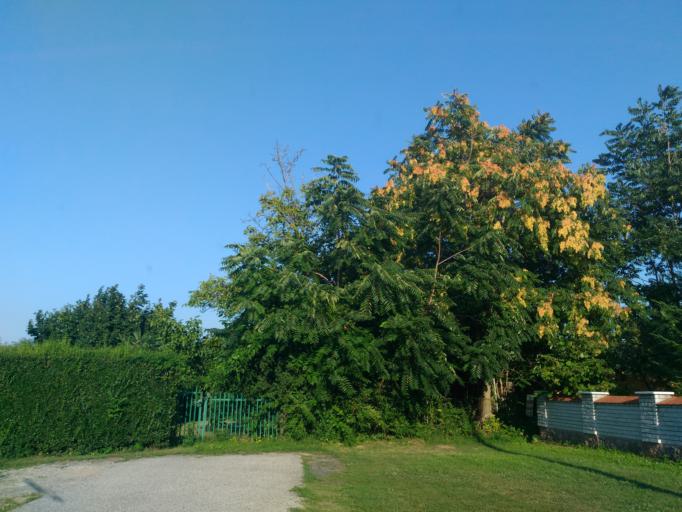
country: HU
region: Somogy
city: Balatonszarszo
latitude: 46.8063
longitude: 17.7847
